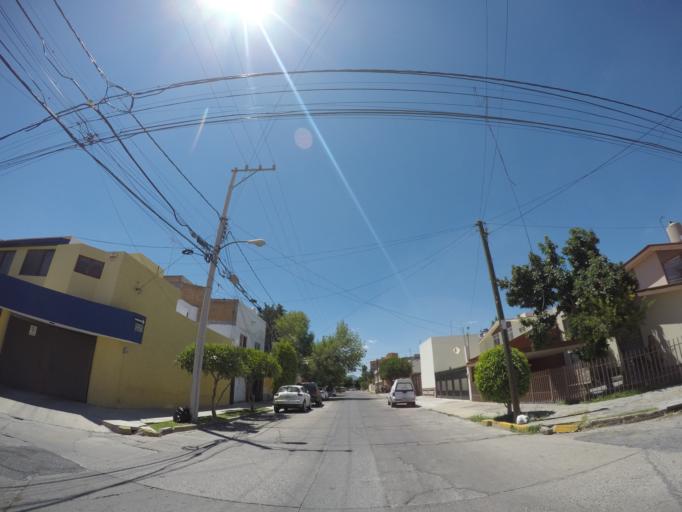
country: MX
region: San Luis Potosi
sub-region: San Luis Potosi
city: San Luis Potosi
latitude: 22.1428
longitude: -101.0039
